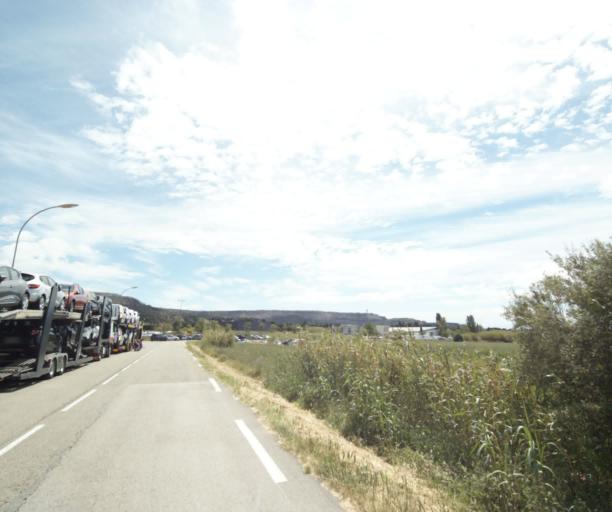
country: FR
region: Provence-Alpes-Cote d'Azur
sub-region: Departement des Bouches-du-Rhone
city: Rognac
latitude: 43.4969
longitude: 5.2253
